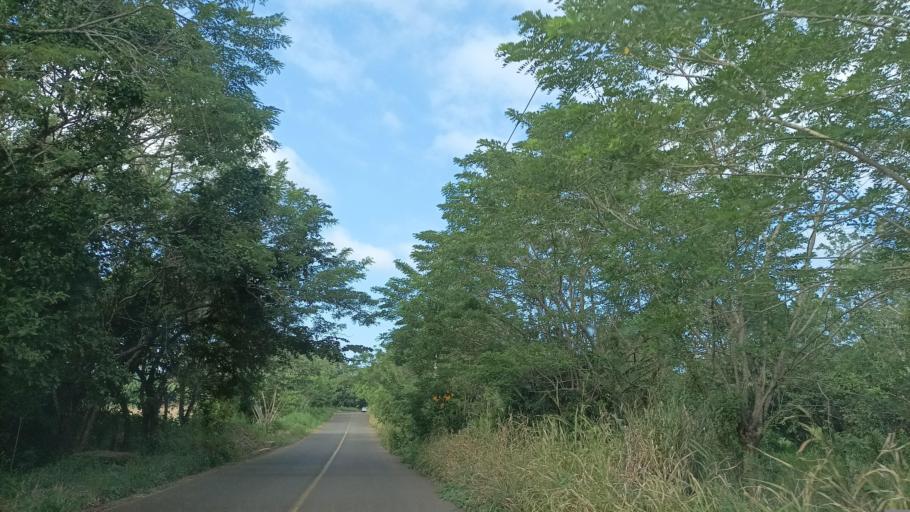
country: MX
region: Veracruz
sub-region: Pajapan
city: Pajapan
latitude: 18.1857
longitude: -94.6882
